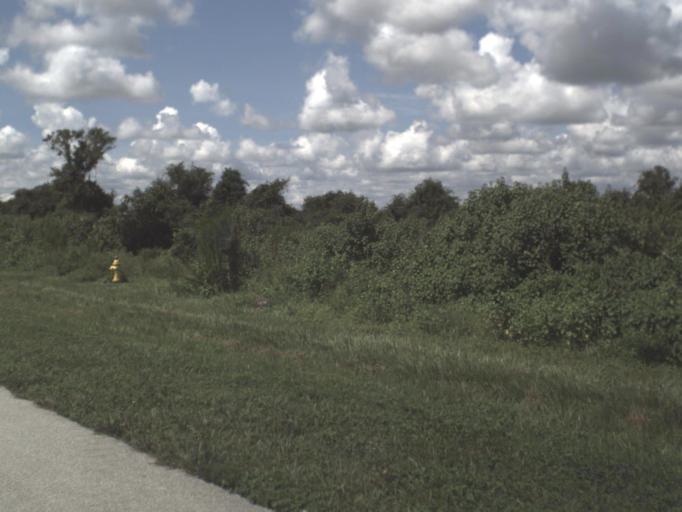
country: US
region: Florida
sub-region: DeSoto County
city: Nocatee
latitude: 27.1261
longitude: -81.9096
